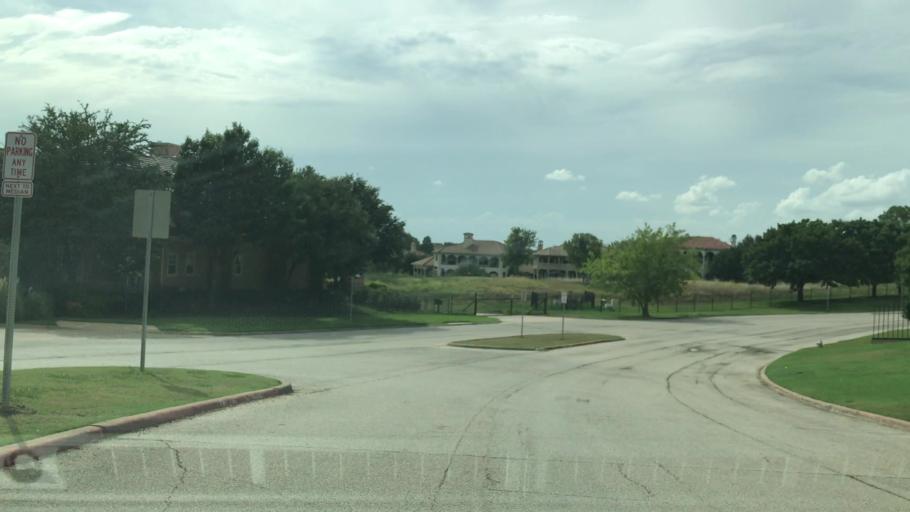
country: US
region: Texas
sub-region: Dallas County
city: Irving
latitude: 32.8669
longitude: -96.9512
